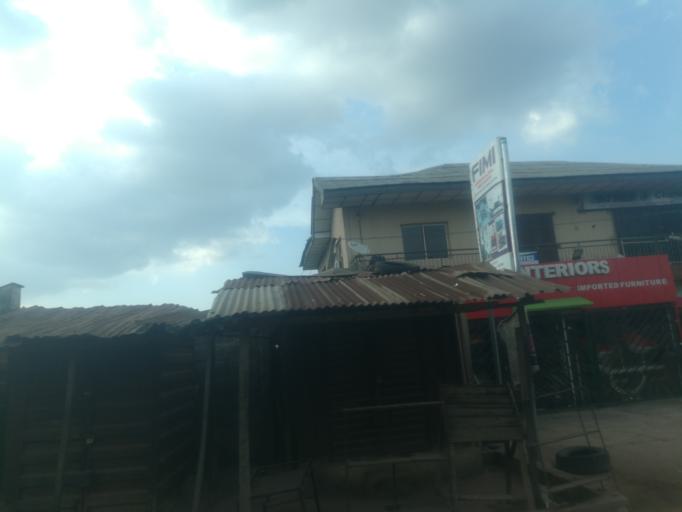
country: NG
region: Ogun
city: Abeokuta
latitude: 7.1316
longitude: 3.3287
